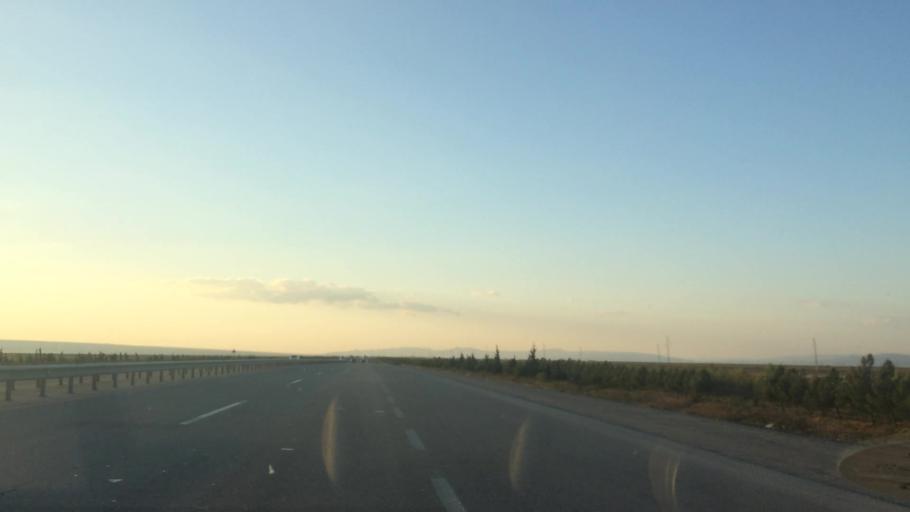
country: AZ
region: Baki
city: Qobustan
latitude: 39.9854
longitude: 49.2101
